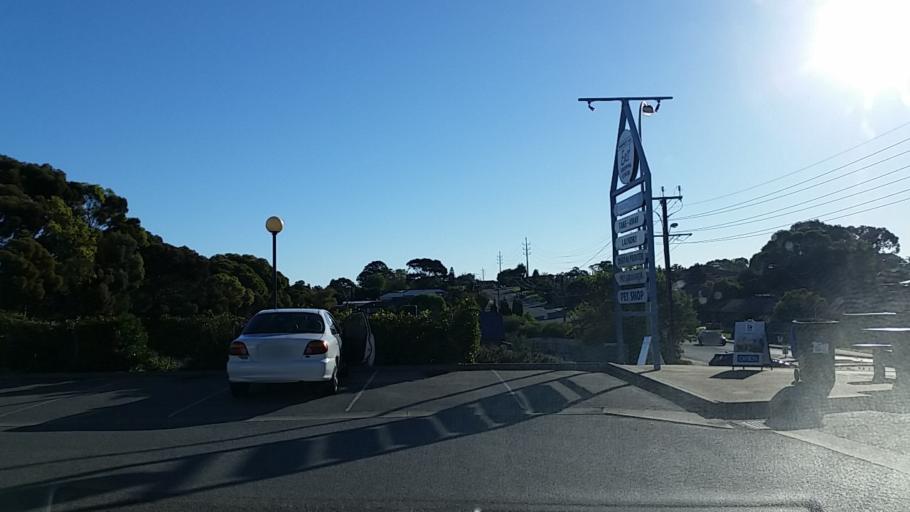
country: AU
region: South Australia
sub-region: Onkaparinga
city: Reynella
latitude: -35.1153
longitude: 138.5360
